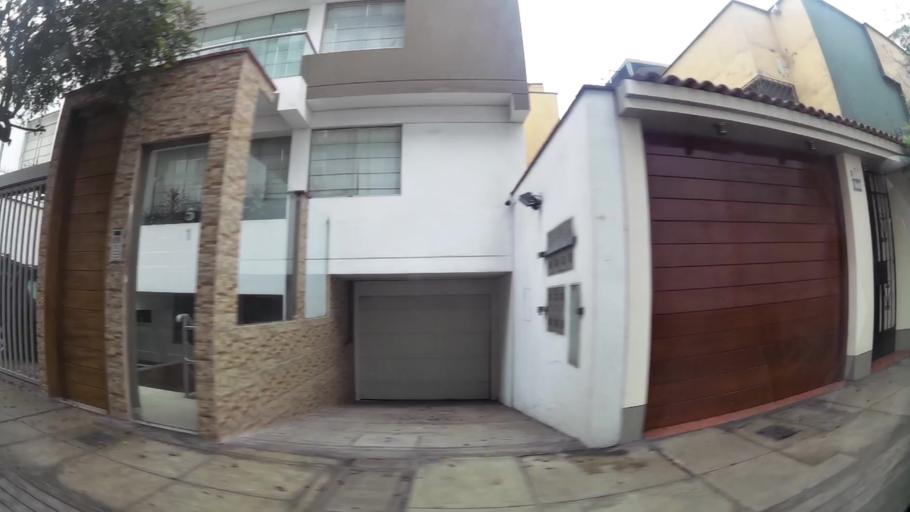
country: PE
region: Lima
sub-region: Lima
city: San Isidro
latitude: -12.1201
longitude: -77.0386
